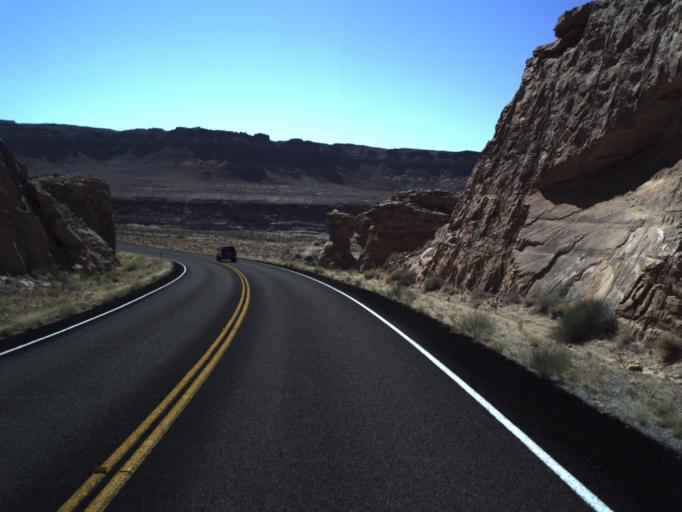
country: US
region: Utah
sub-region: San Juan County
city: Blanding
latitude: 37.8980
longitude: -110.3799
